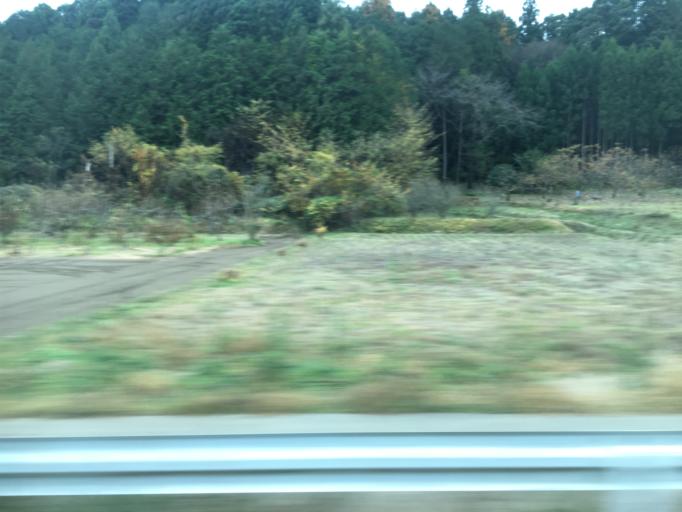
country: JP
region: Ibaraki
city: Kasama
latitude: 36.3765
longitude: 140.2337
